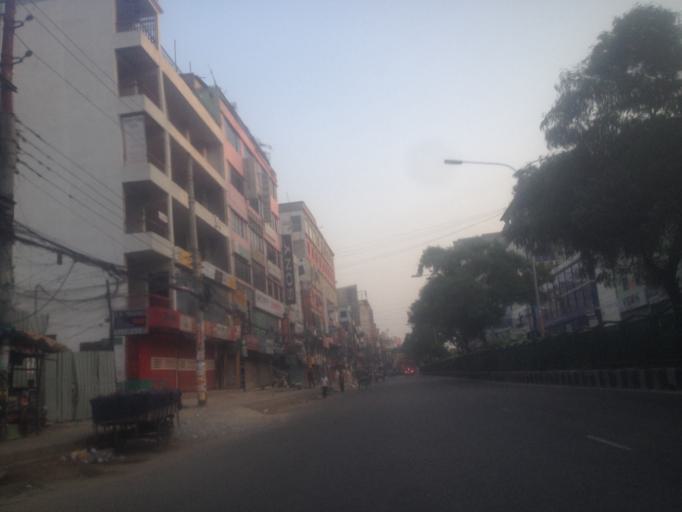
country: BD
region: Dhaka
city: Azimpur
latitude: 23.8044
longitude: 90.3697
